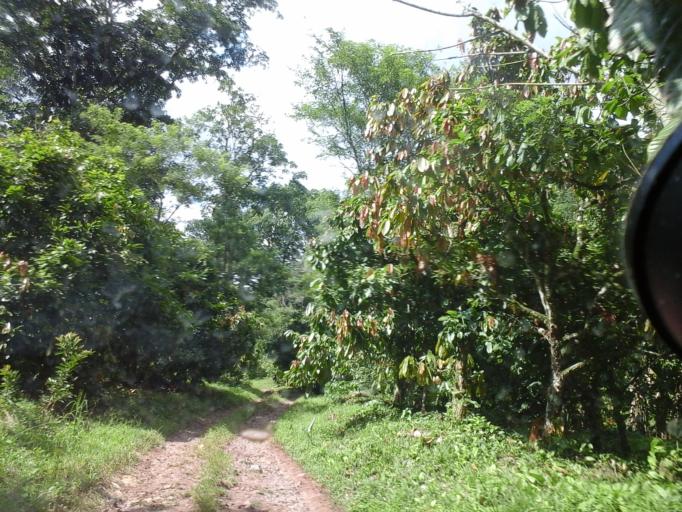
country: CO
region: Cesar
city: San Diego
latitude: 10.2815
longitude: -73.0891
